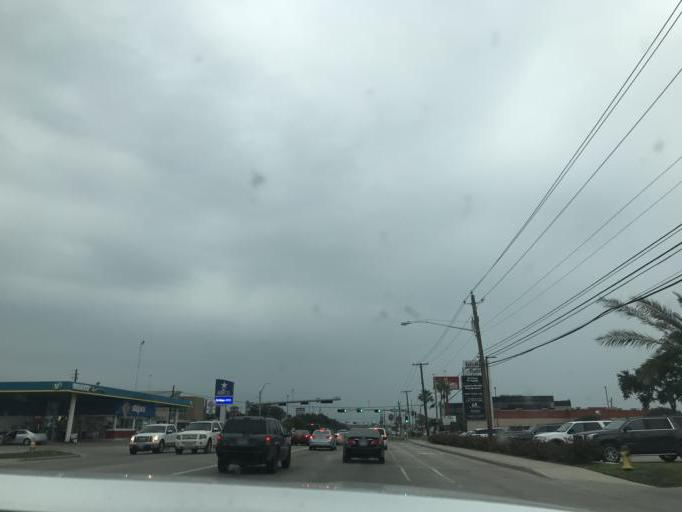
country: US
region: Texas
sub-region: Nueces County
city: Corpus Christi
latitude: 27.7037
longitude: -97.3724
